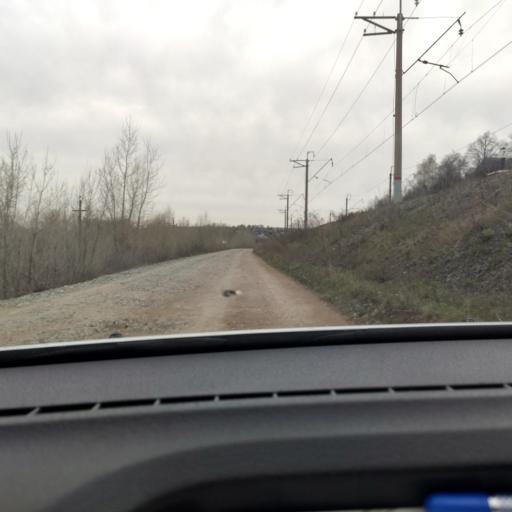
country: RU
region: Bashkortostan
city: Avdon
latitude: 54.6119
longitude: 55.6077
